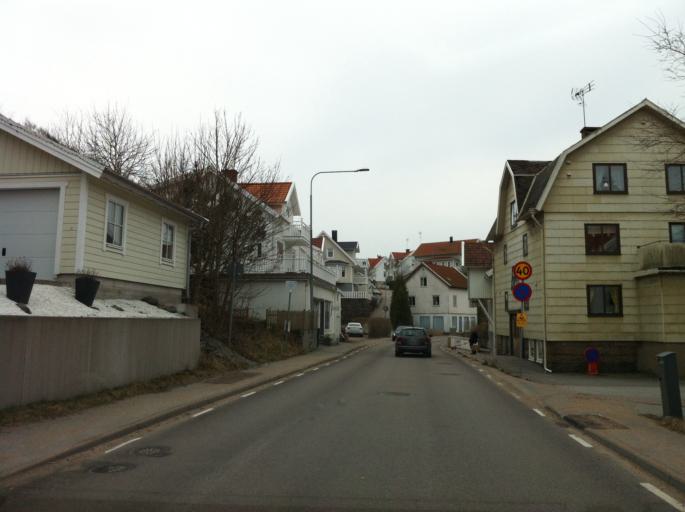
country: SE
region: Vaestra Goetaland
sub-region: Orust
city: Henan
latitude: 58.1697
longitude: 11.7010
